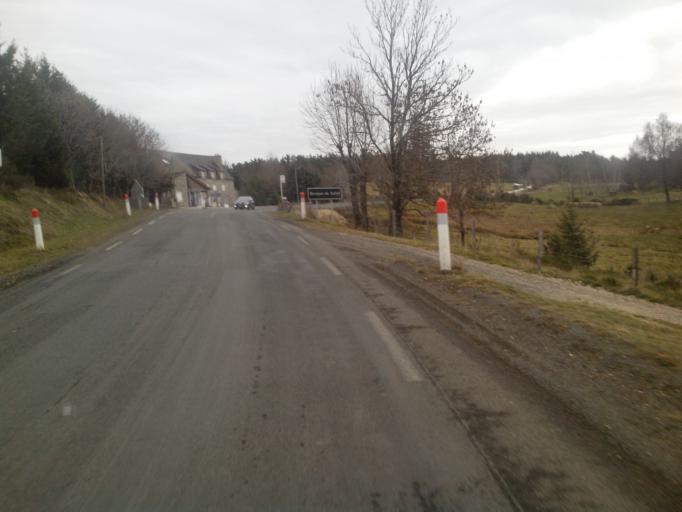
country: FR
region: Languedoc-Roussillon
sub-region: Departement de la Lozere
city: Mende
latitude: 44.6155
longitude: 3.4753
